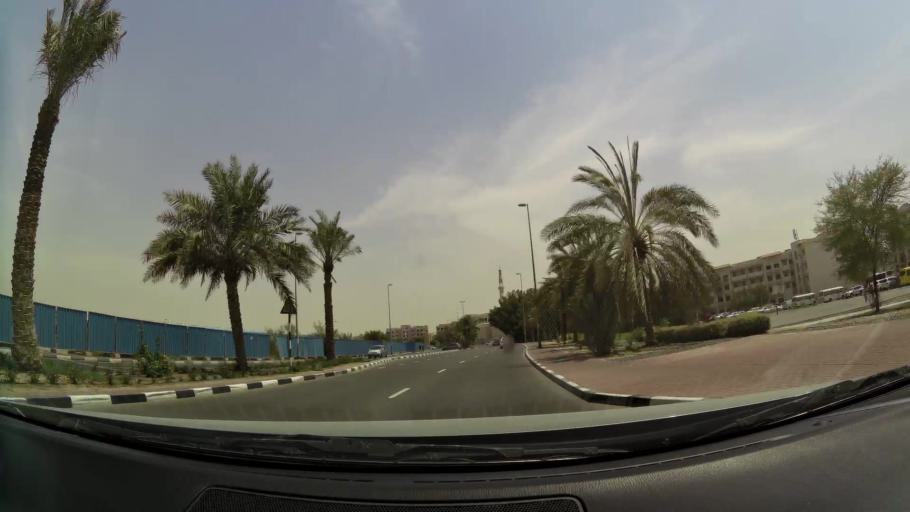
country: AE
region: Ash Shariqah
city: Sharjah
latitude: 25.1703
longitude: 55.4160
